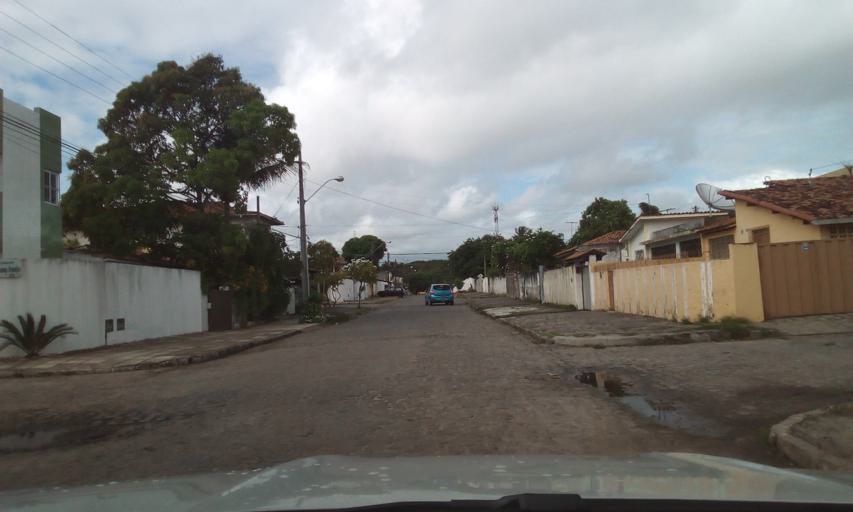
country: BR
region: Paraiba
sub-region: Joao Pessoa
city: Joao Pessoa
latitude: -7.1348
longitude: -34.8502
